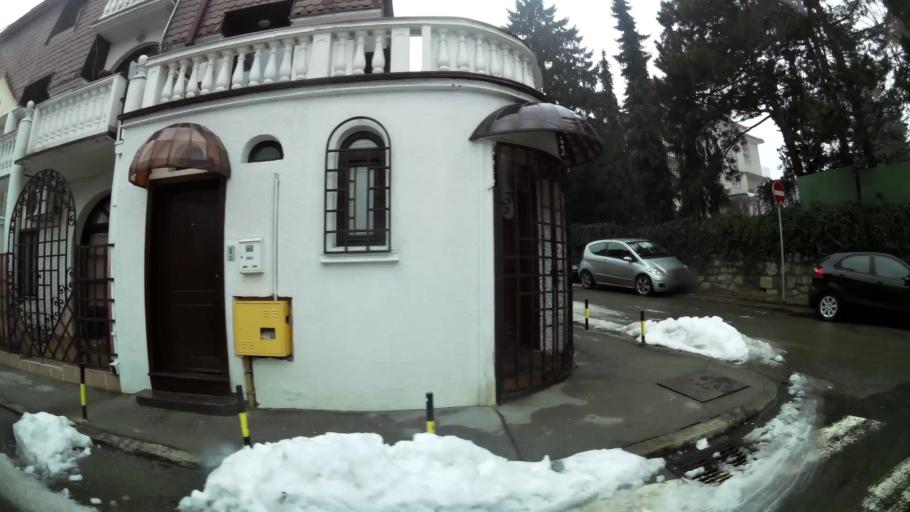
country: RS
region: Central Serbia
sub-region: Belgrade
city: Savski Venac
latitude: 44.7819
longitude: 20.4619
